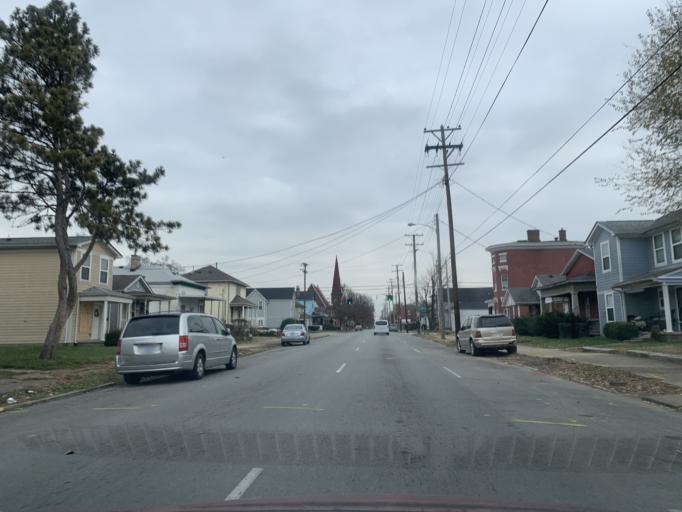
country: US
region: Kentucky
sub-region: Jefferson County
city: Louisville
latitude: 38.2518
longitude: -85.7837
